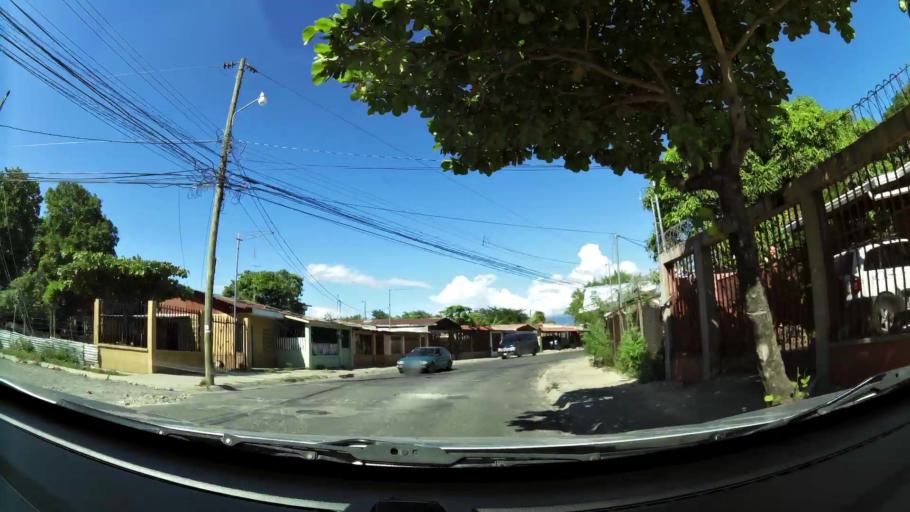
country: CR
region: Guanacaste
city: Liberia
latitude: 10.6360
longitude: -85.4378
